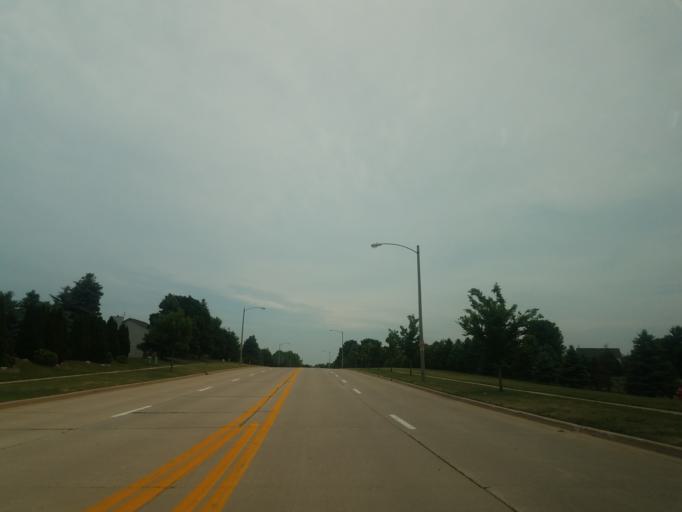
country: US
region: Illinois
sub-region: McLean County
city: Normal
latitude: 40.5162
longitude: -88.9435
